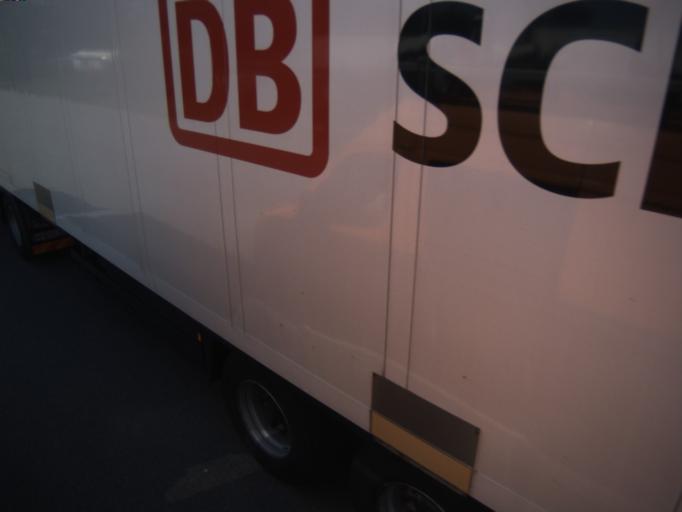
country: SE
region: Skane
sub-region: Helsingborg
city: Gantofta
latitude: 56.0152
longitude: 12.7695
